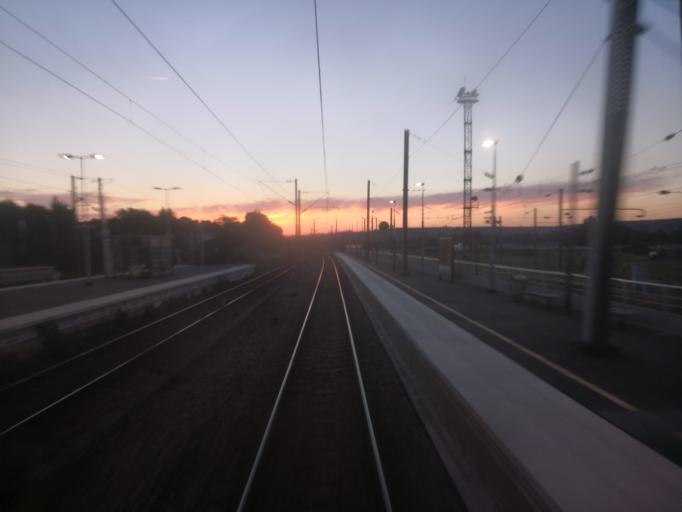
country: FR
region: Ile-de-France
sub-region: Departement des Yvelines
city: Vernouillet
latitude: 48.9818
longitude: 1.9827
